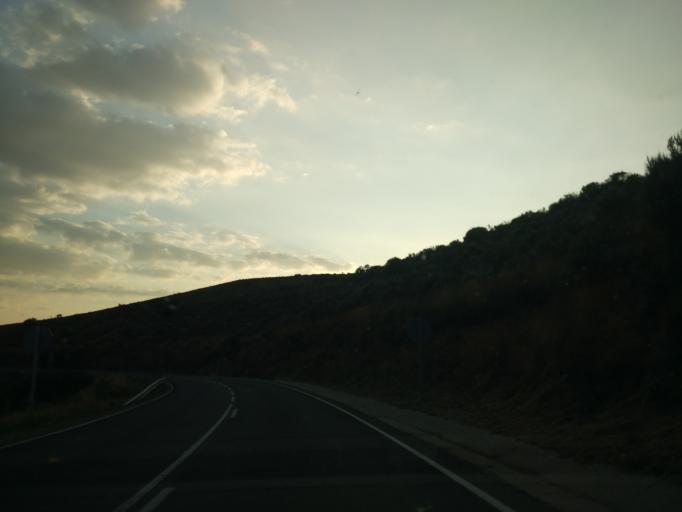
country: ES
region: Castille and Leon
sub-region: Provincia de Avila
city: San Martin del Pimpollar
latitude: 40.3698
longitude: -5.0417
